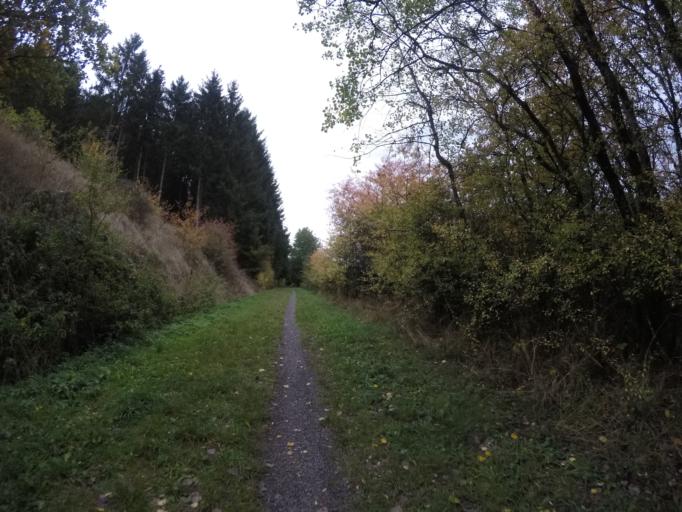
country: BE
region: Wallonia
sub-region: Province du Luxembourg
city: Fauvillers
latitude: 49.8644
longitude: 5.6907
